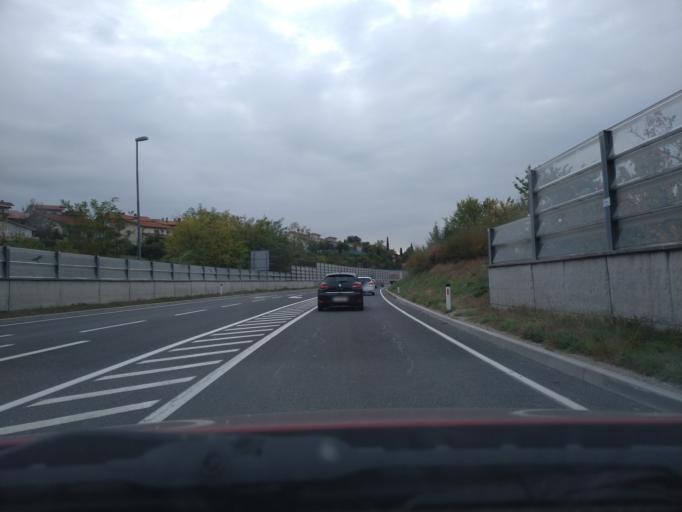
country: SI
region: Nova Gorica
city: Nova Gorica
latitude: 45.9621
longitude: 13.6546
